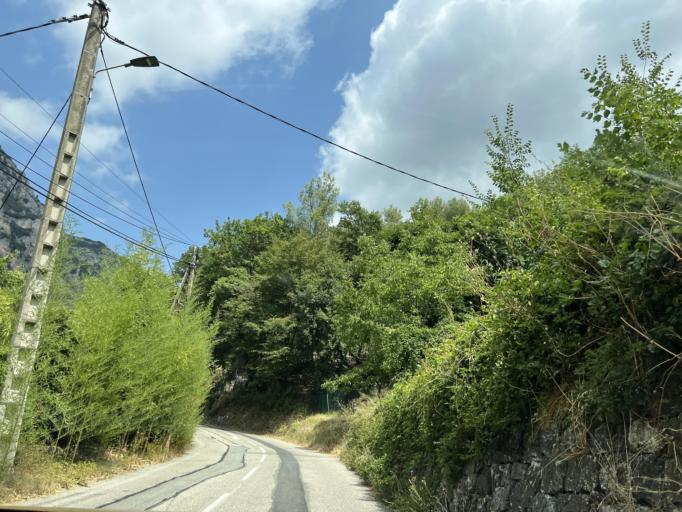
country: FR
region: Provence-Alpes-Cote d'Azur
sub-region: Departement des Alpes-Maritimes
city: Le Rouret
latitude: 43.7186
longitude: 6.9931
